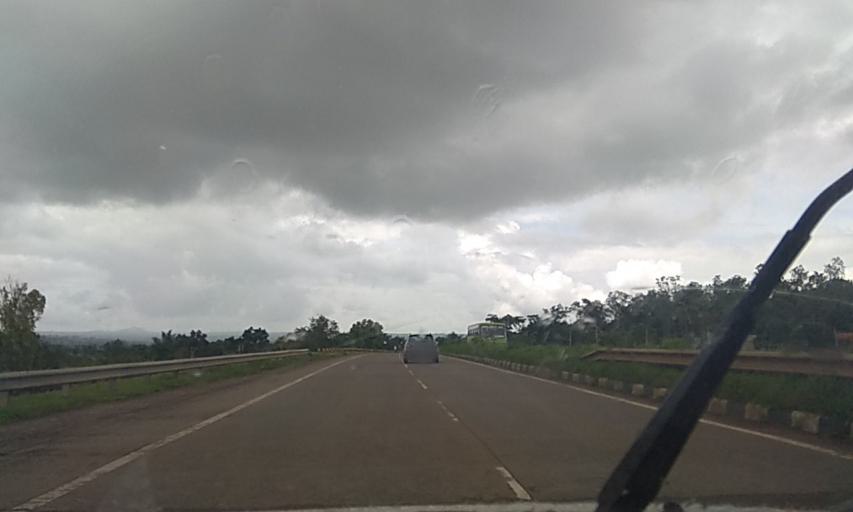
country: IN
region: Karnataka
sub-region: Belgaum
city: Sankeshwar
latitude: 16.2798
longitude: 74.4482
